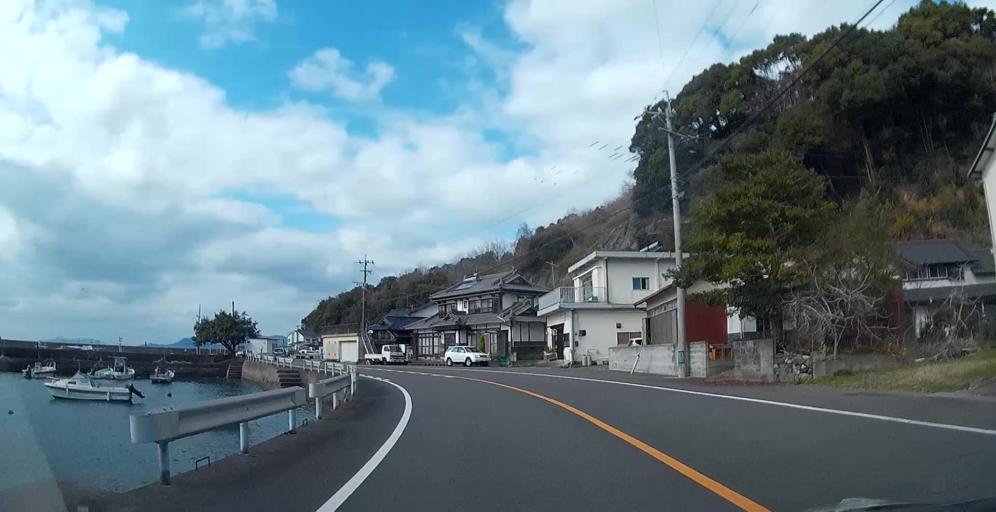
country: JP
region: Kumamoto
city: Minamata
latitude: 32.3115
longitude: 130.4720
